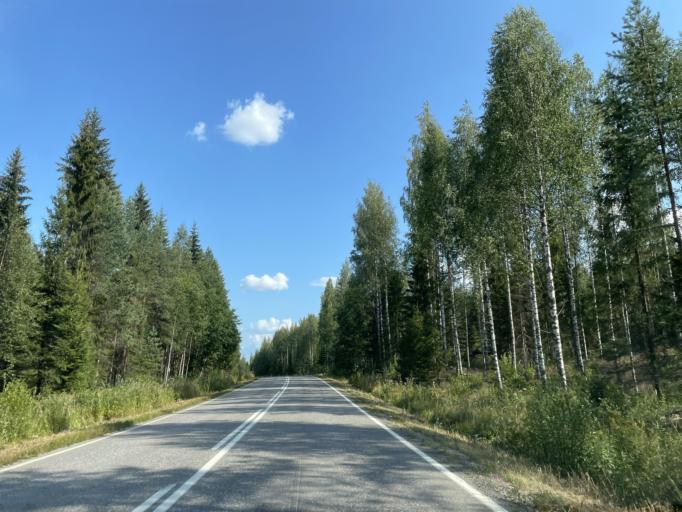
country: FI
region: Central Finland
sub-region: Saarijaervi-Viitasaari
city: Pihtipudas
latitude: 63.3665
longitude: 25.6928
